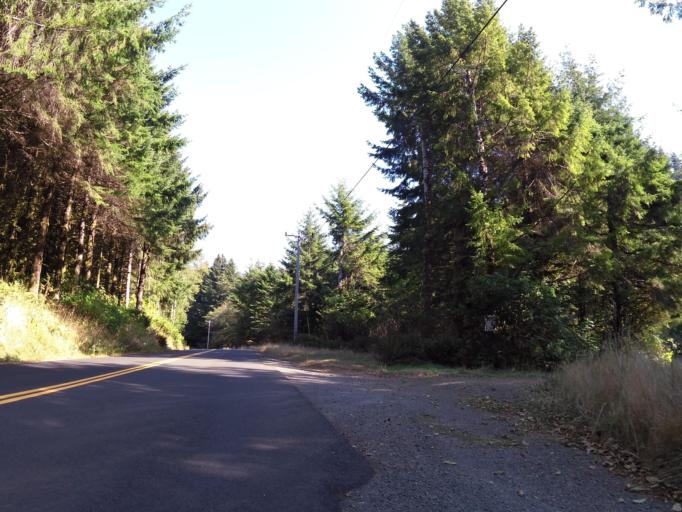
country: US
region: Oregon
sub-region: Lincoln County
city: Rose Lodge
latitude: 45.0836
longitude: -123.9500
